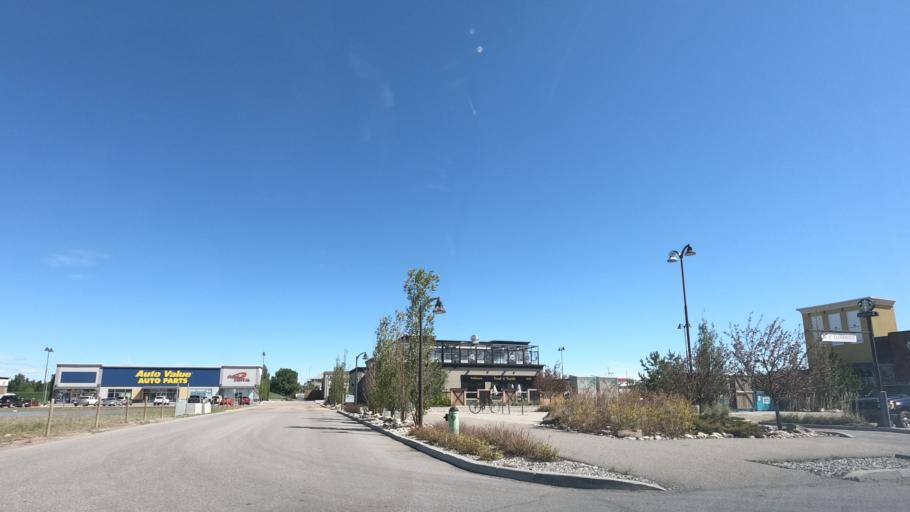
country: CA
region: Alberta
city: Airdrie
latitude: 51.2692
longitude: -113.9954
